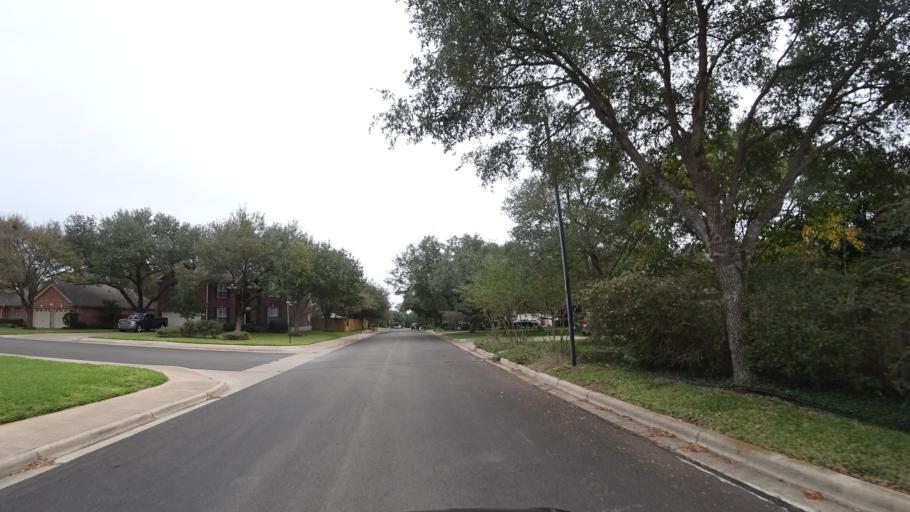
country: US
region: Texas
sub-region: Travis County
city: Shady Hollow
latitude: 30.1857
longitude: -97.8932
